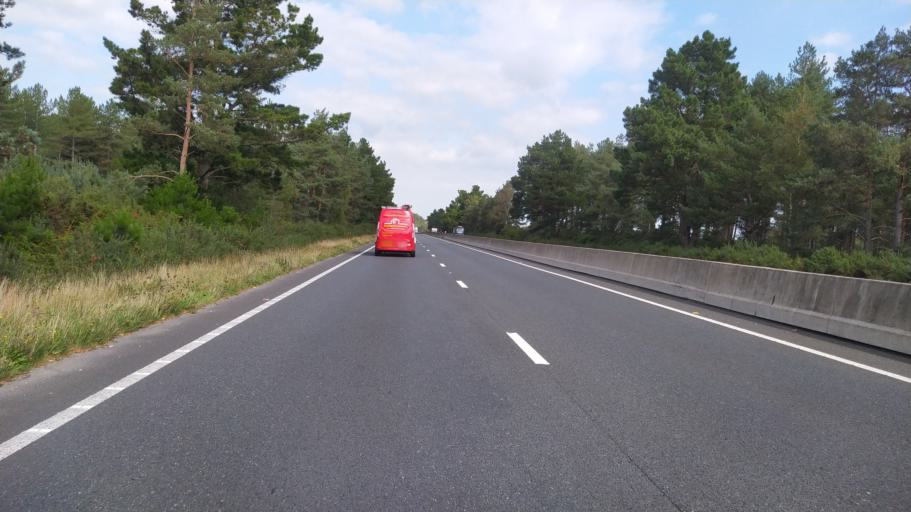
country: GB
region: England
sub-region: Dorset
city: St Leonards
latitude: 50.7914
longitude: -1.8148
